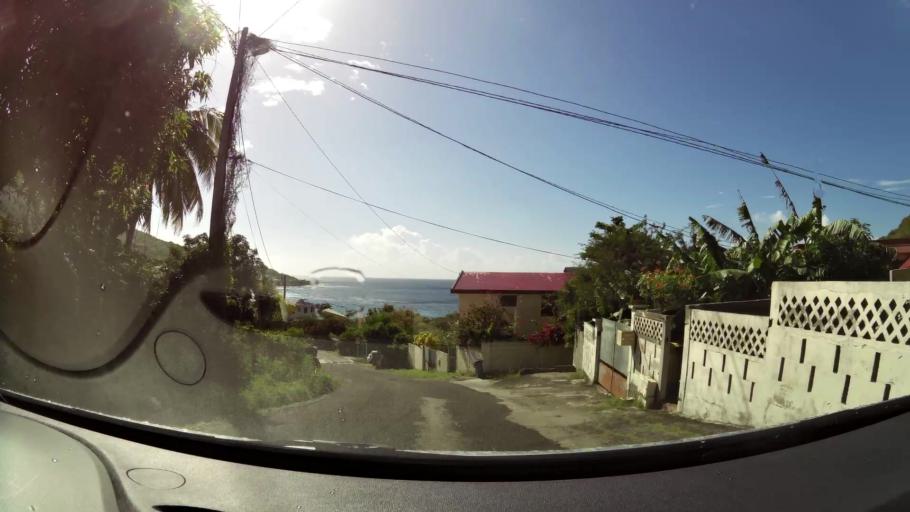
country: MQ
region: Martinique
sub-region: Martinique
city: Les Trois-Ilets
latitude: 14.4715
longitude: -61.0719
